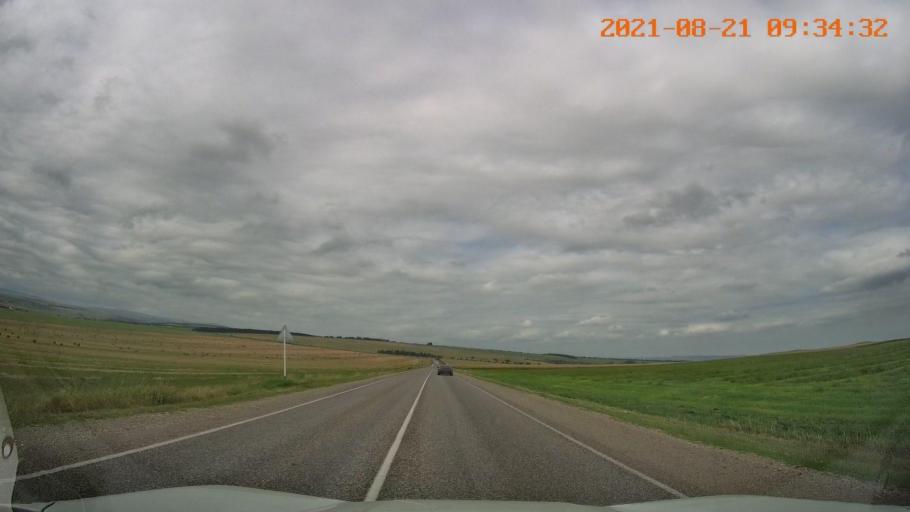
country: RU
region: Stavropol'skiy
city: Yutsa
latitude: 43.9926
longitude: 42.9720
